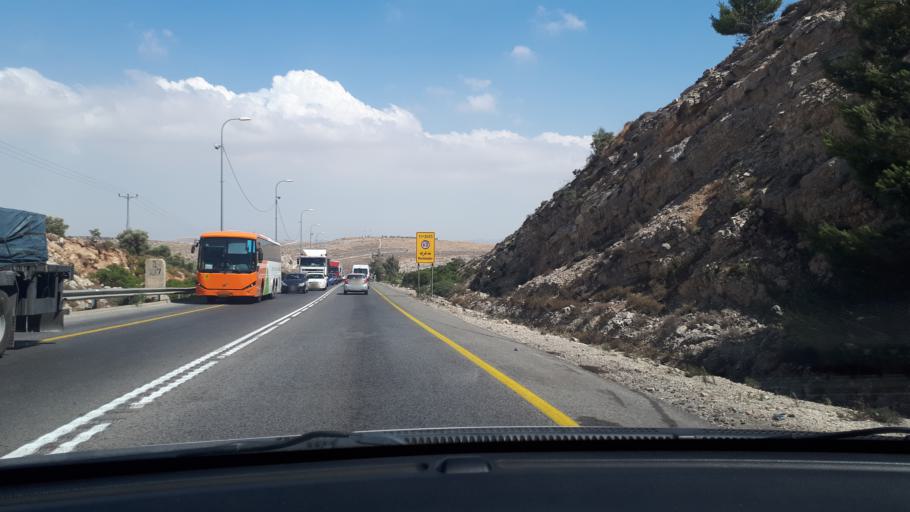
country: PS
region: West Bank
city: Burqah
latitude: 31.9054
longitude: 35.2559
